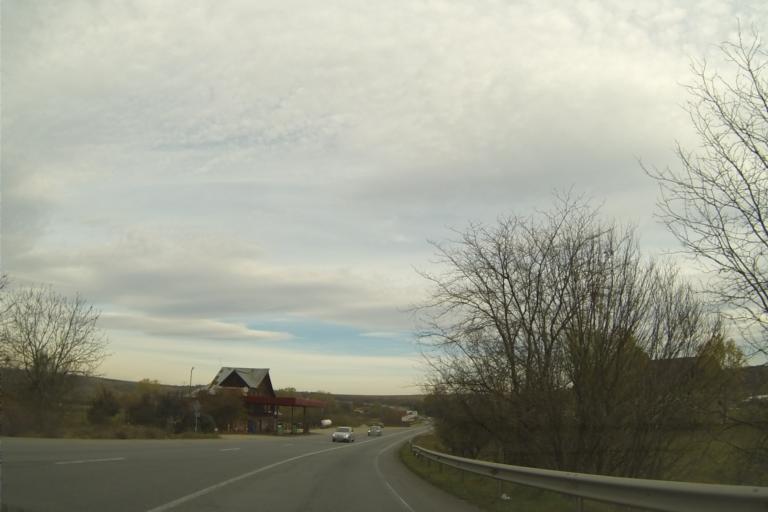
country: RO
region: Olt
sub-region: Comuna Valea Mare
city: Valea Mare
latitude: 44.4806
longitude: 24.4351
